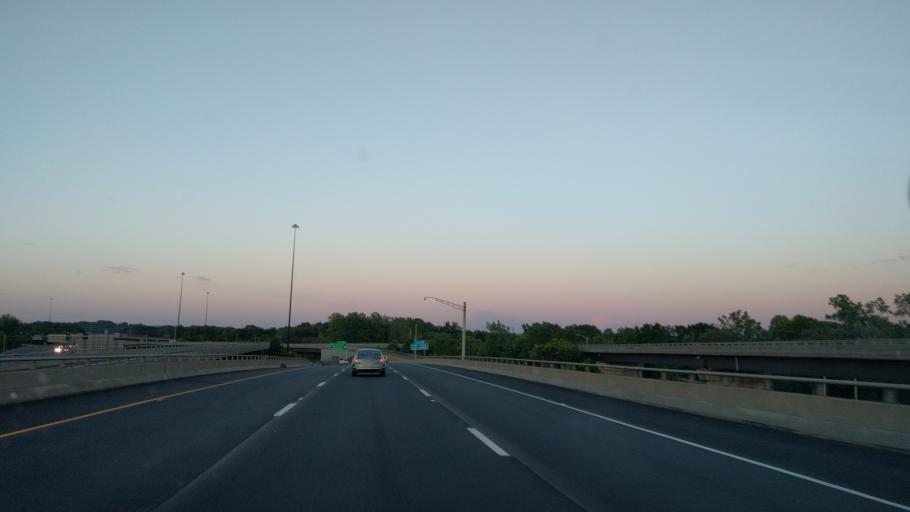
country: US
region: Connecticut
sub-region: Hartford County
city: East Hartford
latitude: 41.7632
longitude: -72.6354
